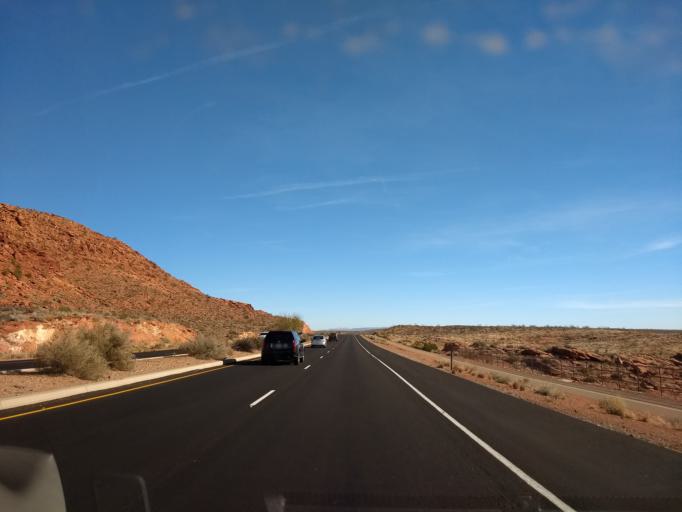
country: US
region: Utah
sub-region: Washington County
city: Saint George
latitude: 37.1340
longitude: -113.5929
